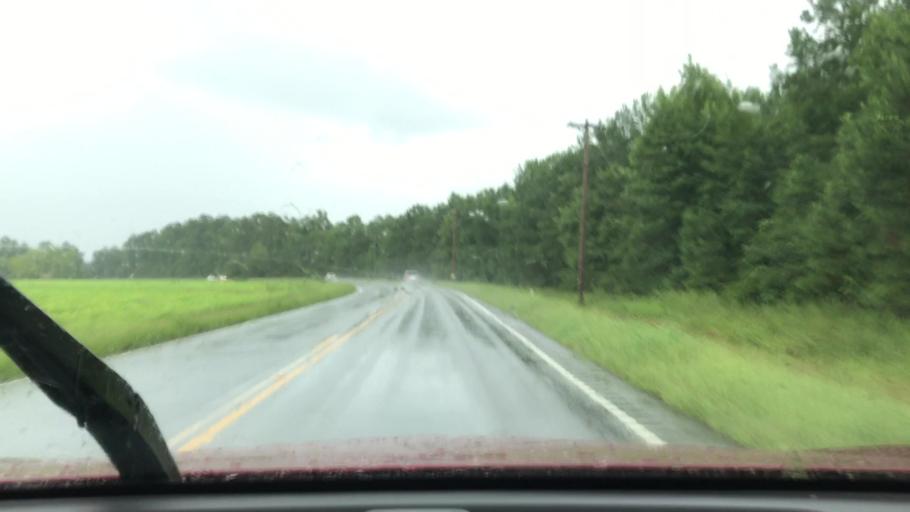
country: US
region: South Carolina
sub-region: Horry County
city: Socastee
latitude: 33.7224
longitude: -79.0872
